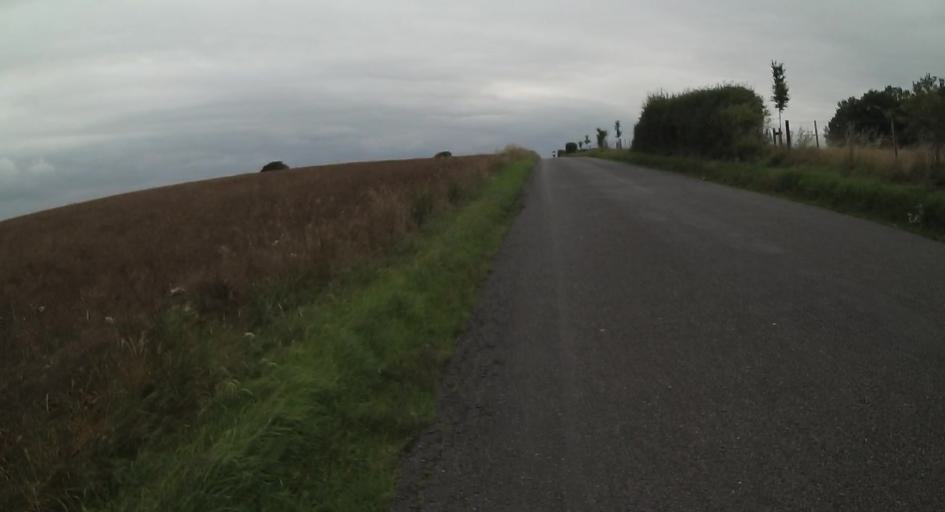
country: GB
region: England
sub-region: Hampshire
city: Bishops Waltham
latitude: 51.0301
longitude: -1.2097
